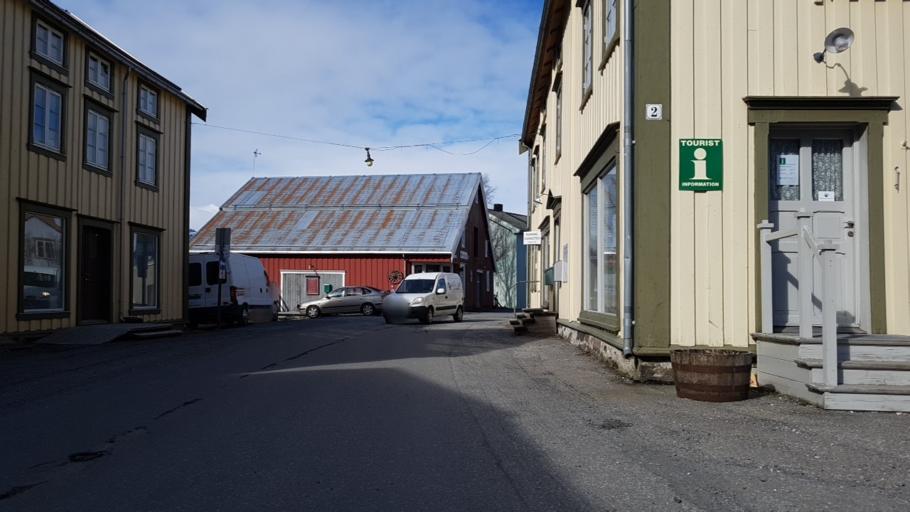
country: NO
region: Nordland
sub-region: Vefsn
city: Mosjoen
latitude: 65.8386
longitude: 13.1872
